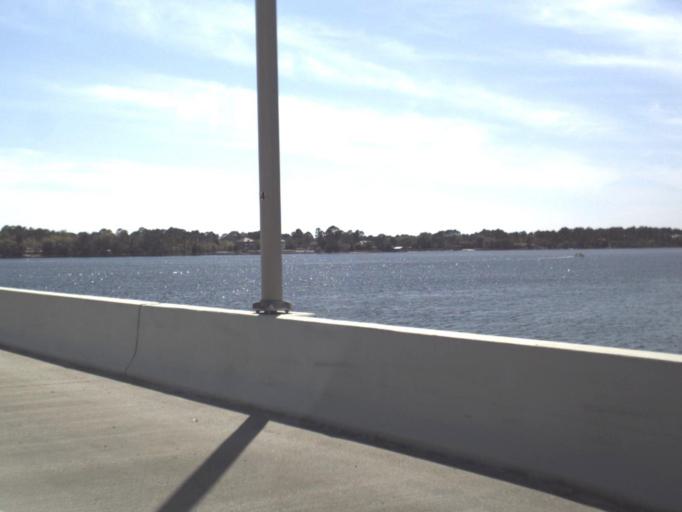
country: US
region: Florida
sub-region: Bay County
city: Lynn Haven
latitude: 30.2624
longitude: -85.6466
